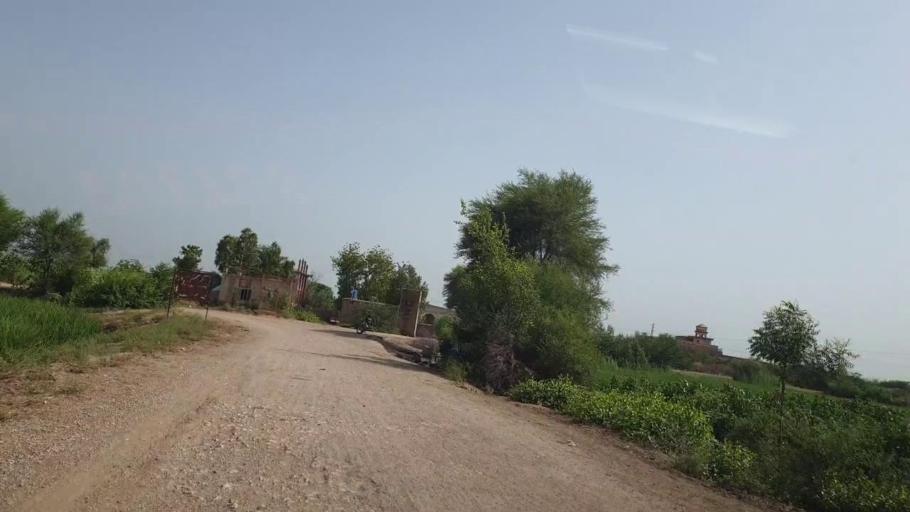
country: PK
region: Sindh
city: Sakrand
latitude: 26.2913
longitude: 68.2265
